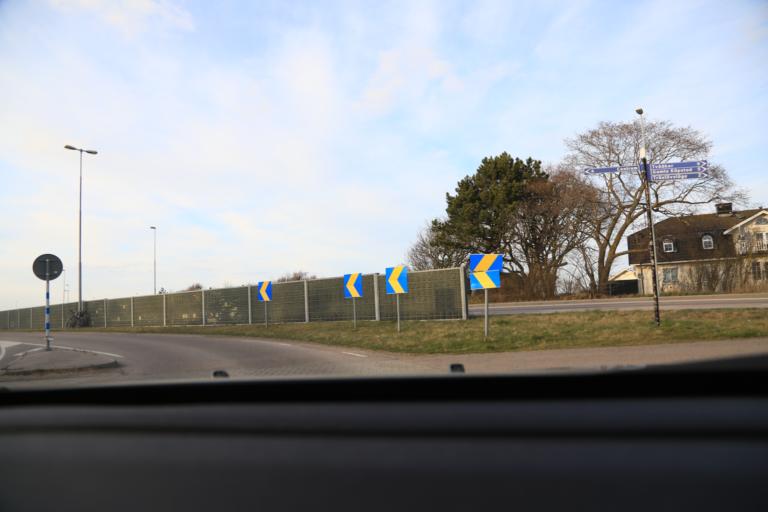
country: SE
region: Halland
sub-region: Varbergs Kommun
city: Traslovslage
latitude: 57.0780
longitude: 12.2796
